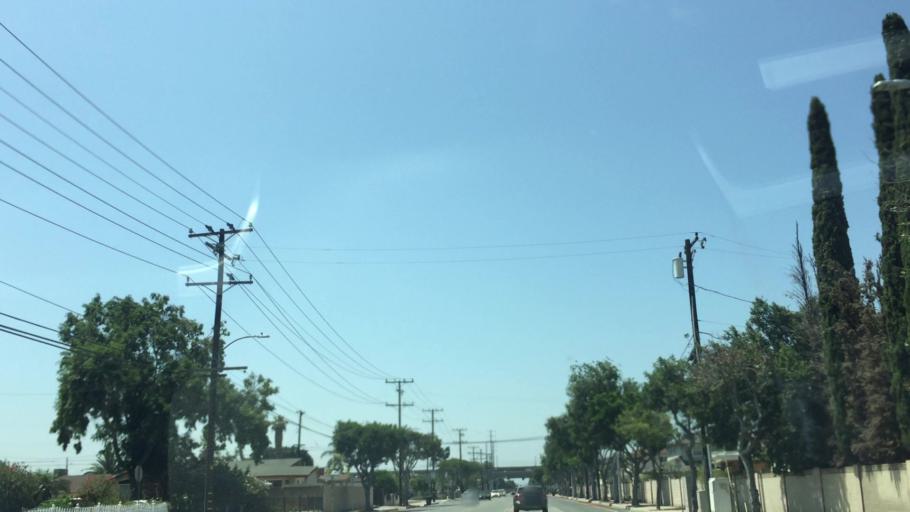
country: US
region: California
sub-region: Orange County
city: Garden Grove
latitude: 33.7705
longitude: -117.9292
